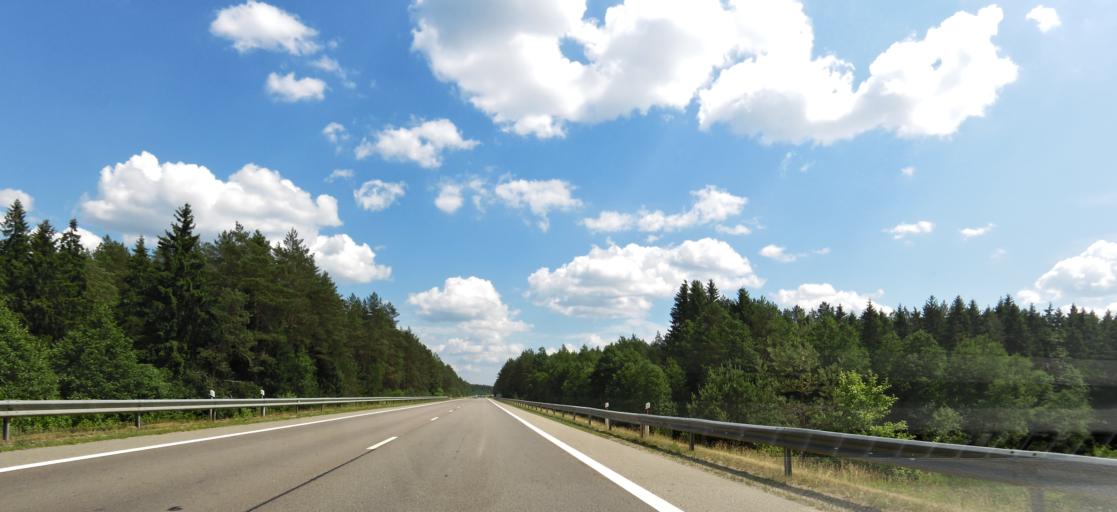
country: LT
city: Skaidiskes
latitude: 54.5948
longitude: 25.5326
